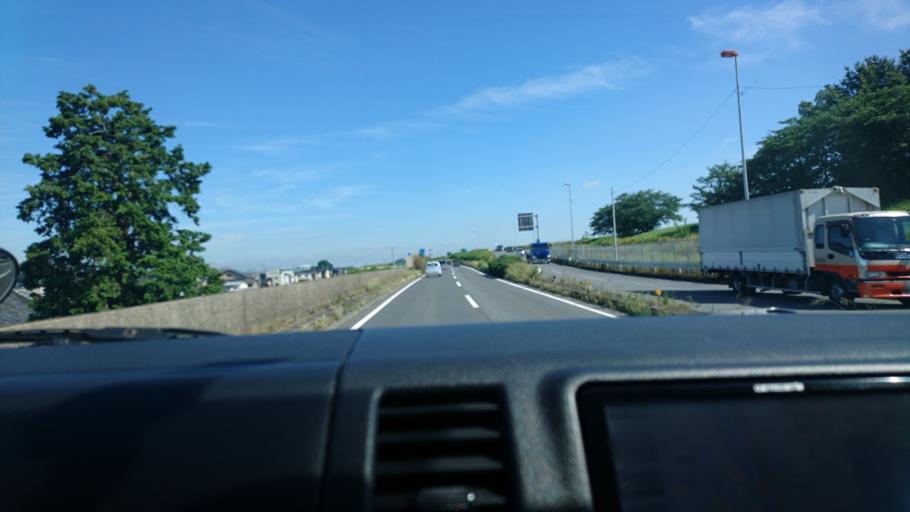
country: JP
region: Saitama
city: Kurihashi
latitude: 36.1363
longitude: 139.7058
